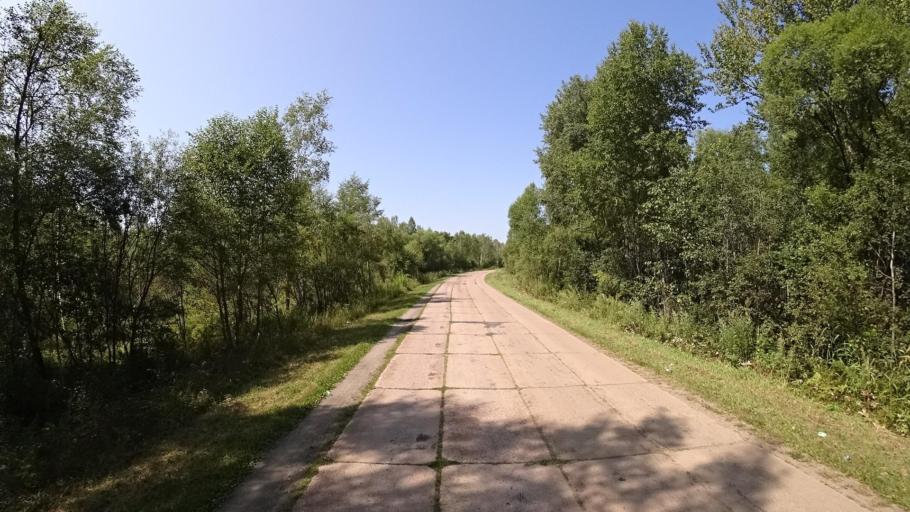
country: RU
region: Khabarovsk Krai
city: Khor
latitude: 47.9784
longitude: 135.1020
